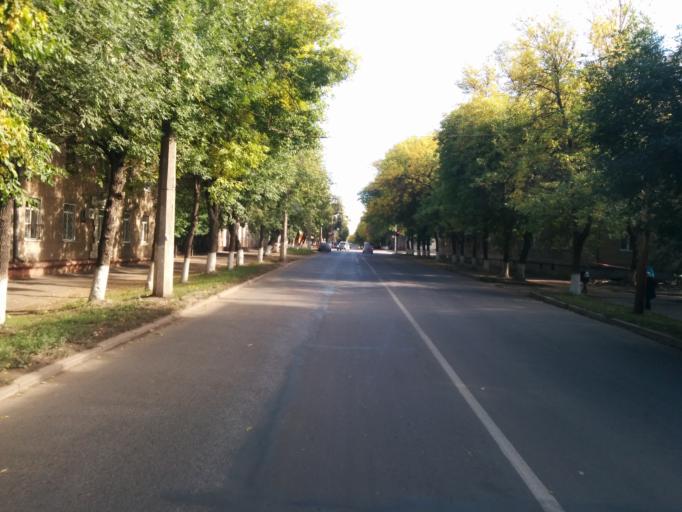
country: RU
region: Bashkortostan
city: Ufa
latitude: 54.8236
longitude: 56.0659
